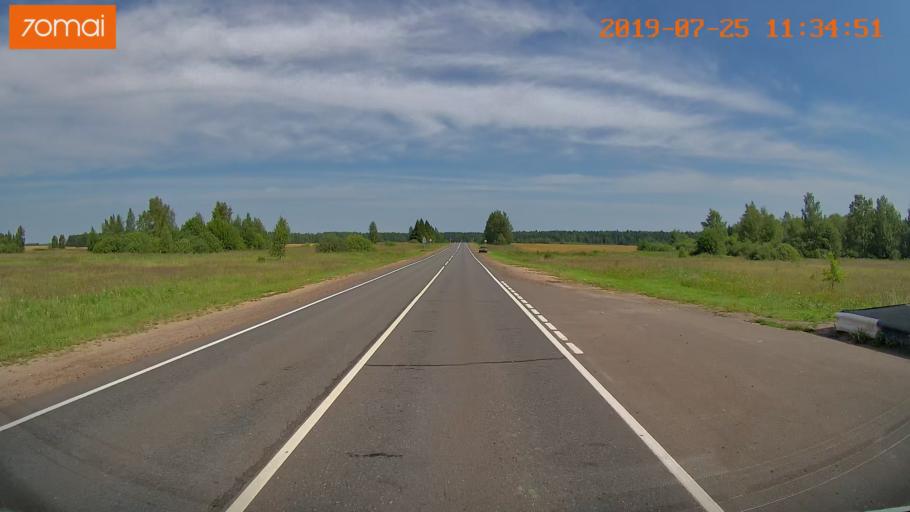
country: RU
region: Ivanovo
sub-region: Privolzhskiy Rayon
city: Ples
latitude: 57.4045
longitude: 41.4199
